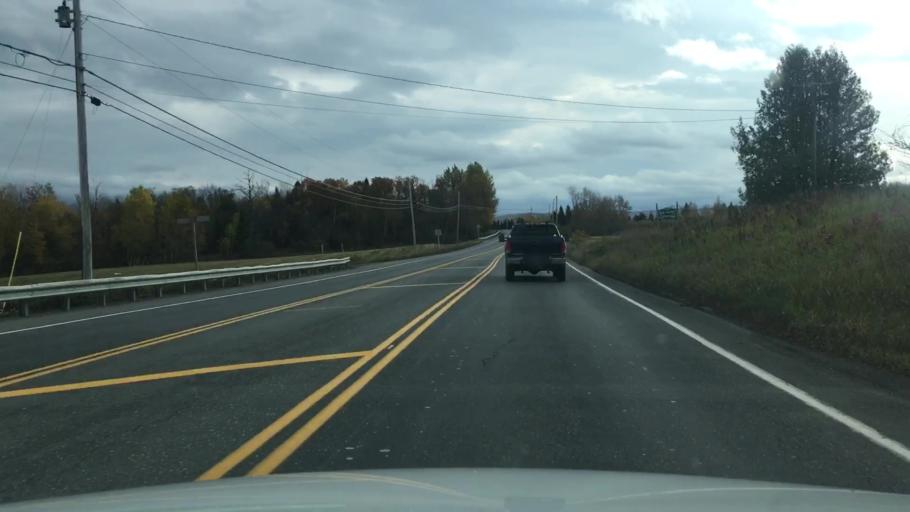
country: US
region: Maine
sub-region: Aroostook County
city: Easton
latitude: 46.5676
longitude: -67.9496
